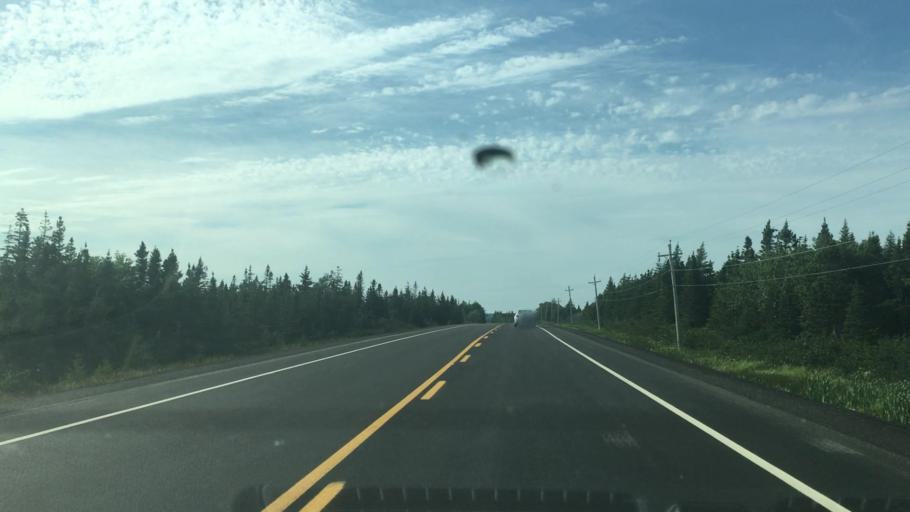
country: CA
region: Nova Scotia
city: Sydney Mines
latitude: 46.8463
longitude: -60.4112
